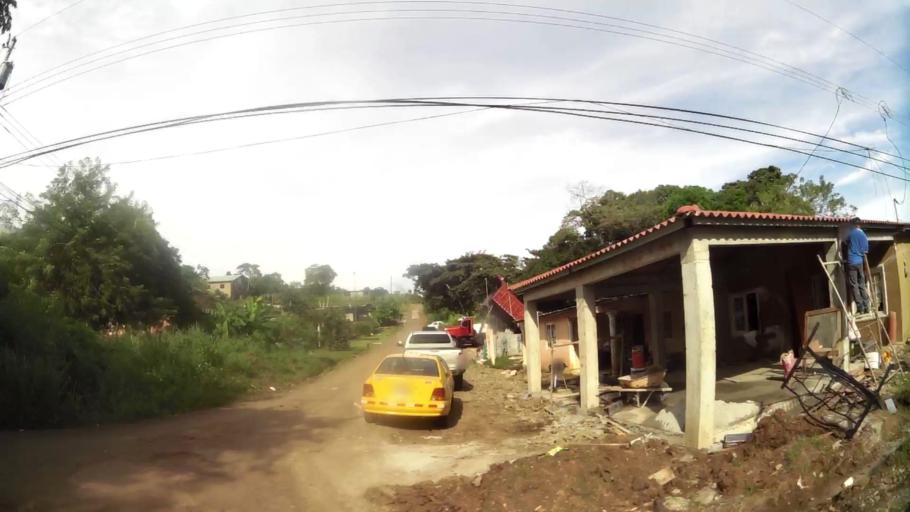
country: PA
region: Panama
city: La Chorrera
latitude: 8.8859
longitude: -79.7694
